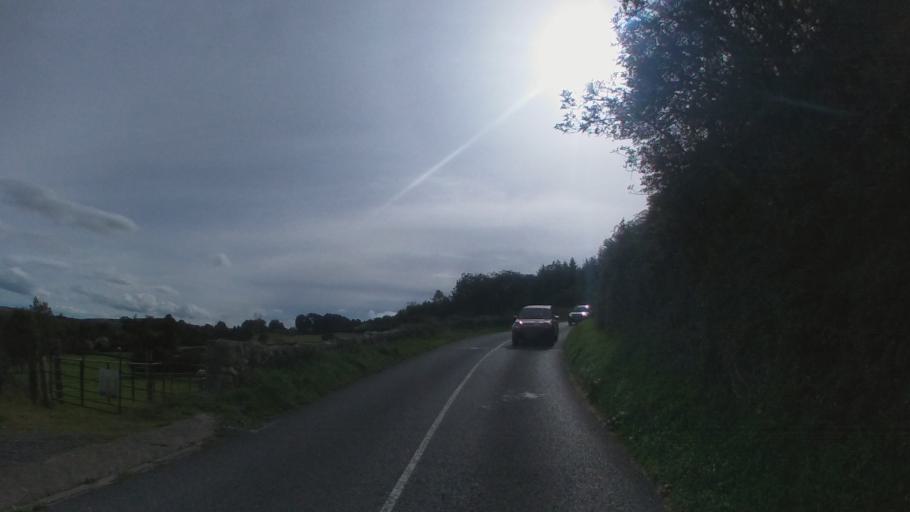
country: IE
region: Leinster
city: Sandyford
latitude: 53.2532
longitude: -6.2194
